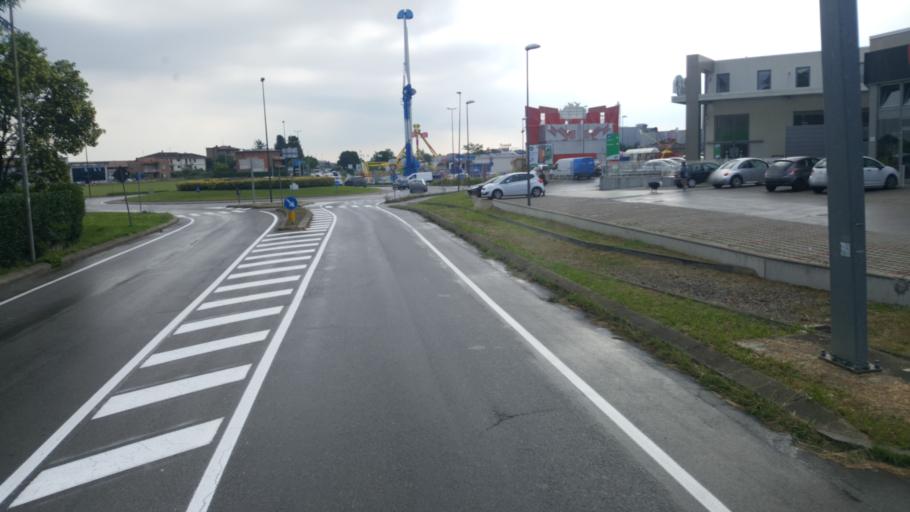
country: IT
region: Emilia-Romagna
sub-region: Provincia di Modena
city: Vignola
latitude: 44.4891
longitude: 11.0011
